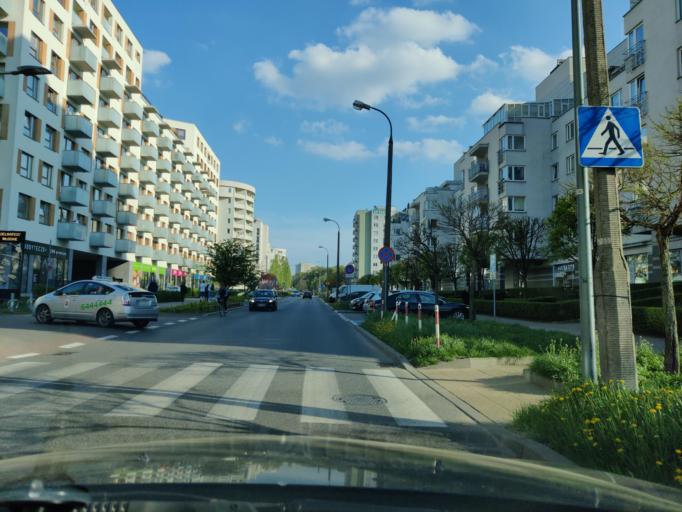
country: PL
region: Masovian Voivodeship
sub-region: Warszawa
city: Ursynow
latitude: 52.1462
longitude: 21.0561
